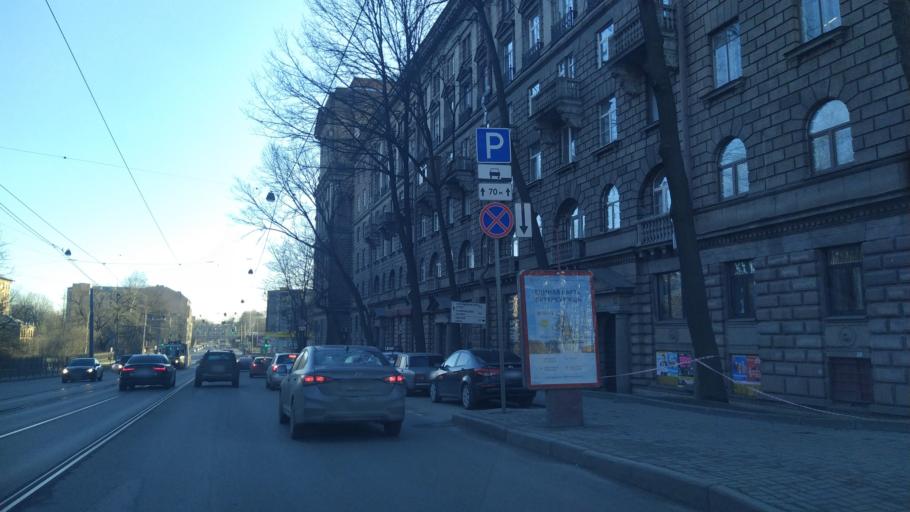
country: RU
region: Leningrad
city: Svetlanovskiy
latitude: 59.9962
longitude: 30.3305
